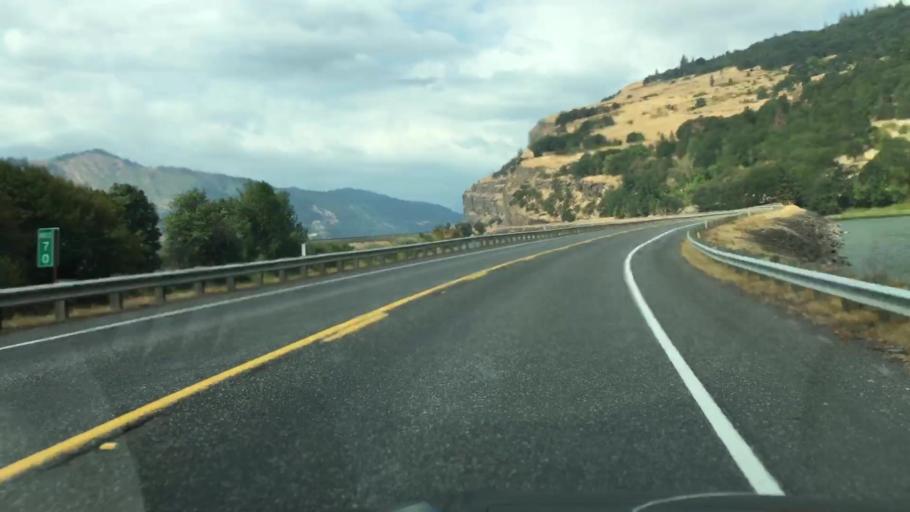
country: US
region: Washington
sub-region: Klickitat County
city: White Salmon
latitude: 45.6981
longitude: -121.3982
